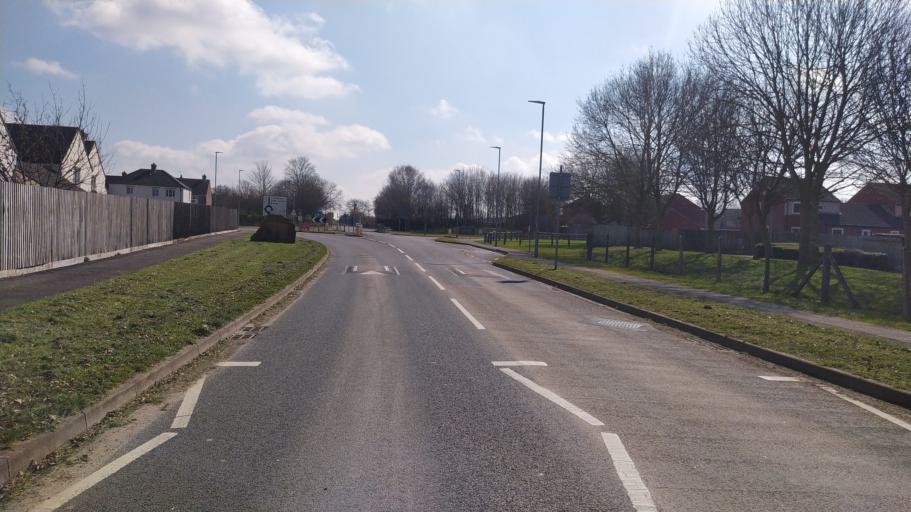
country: GB
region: England
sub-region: Somerset
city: Ilchester
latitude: 51.0121
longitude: -2.6820
